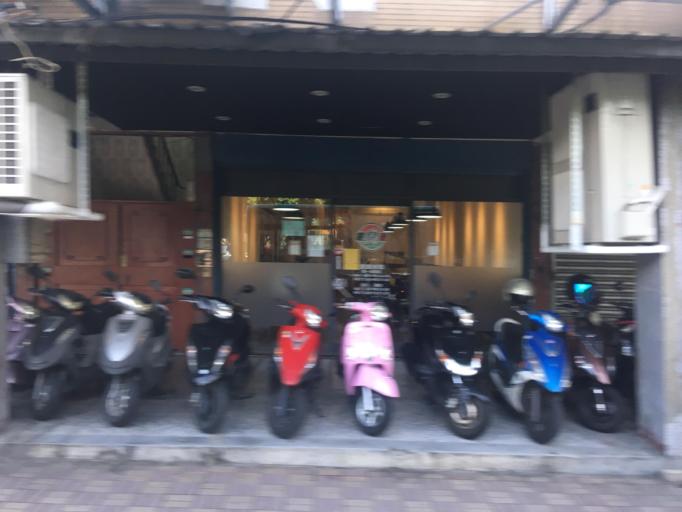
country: TW
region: Taipei
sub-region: Taipei
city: Banqiao
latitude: 25.0458
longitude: 121.4261
